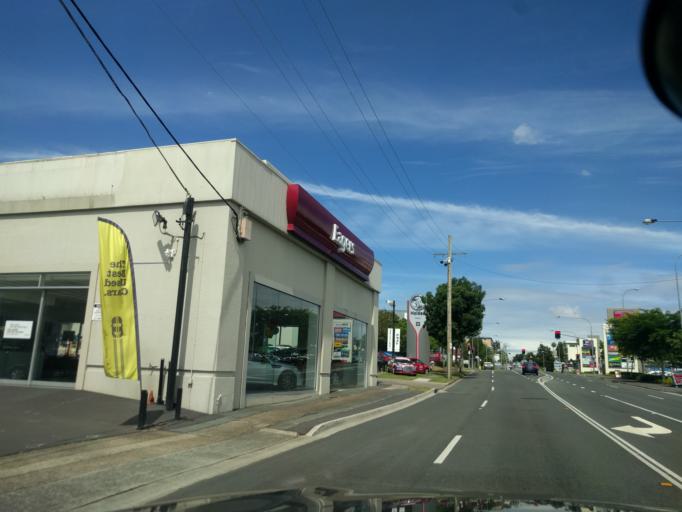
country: AU
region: Queensland
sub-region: Brisbane
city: Windsor
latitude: -27.4369
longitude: 153.0232
